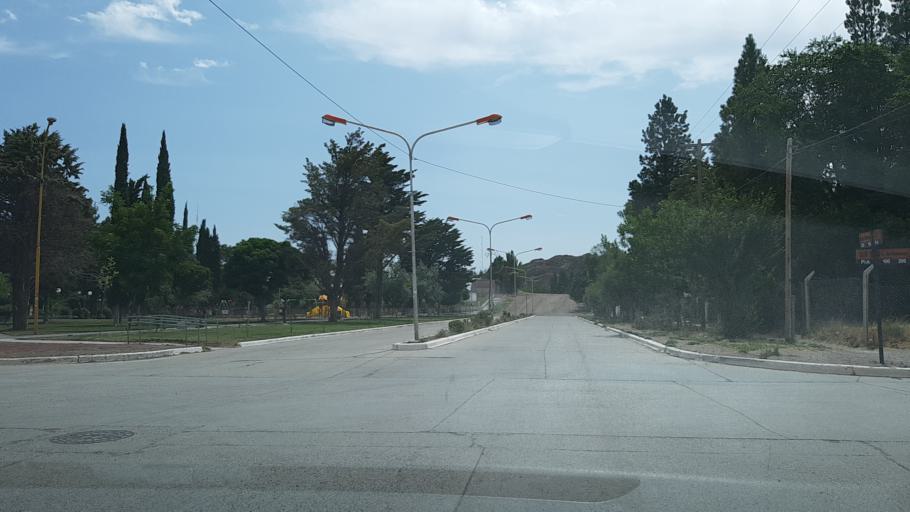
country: AR
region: Neuquen
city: Piedra del Aguila
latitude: -40.0494
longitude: -70.0751
